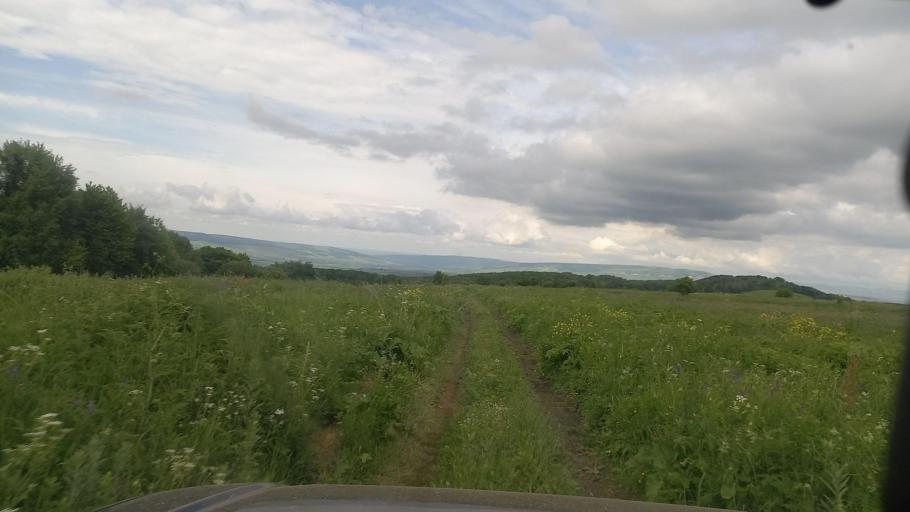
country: RU
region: Krasnodarskiy
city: Peredovaya
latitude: 44.0432
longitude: 41.3334
